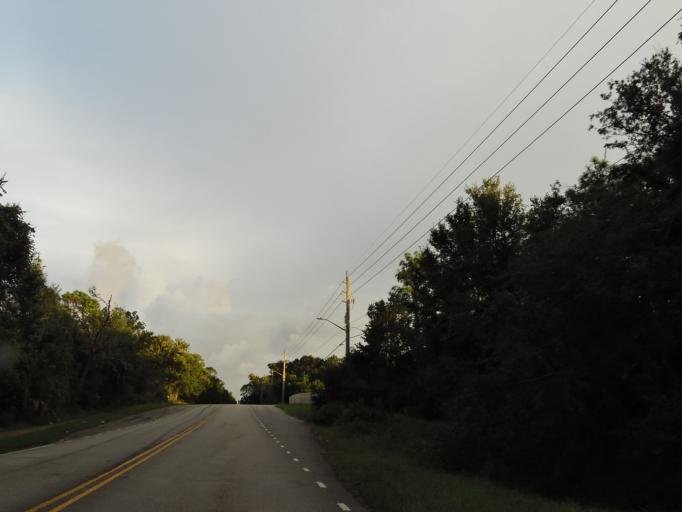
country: US
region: Florida
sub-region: Duval County
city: Atlantic Beach
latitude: 30.3718
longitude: -81.4870
